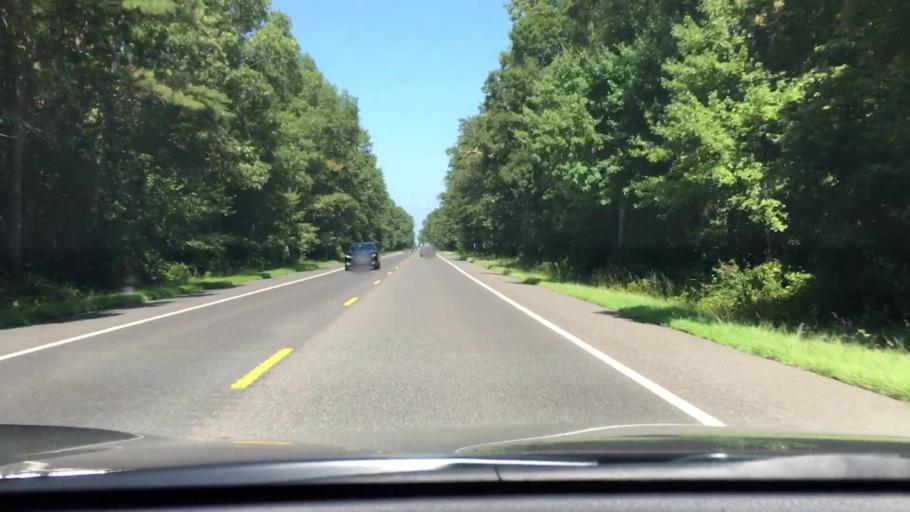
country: US
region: New Jersey
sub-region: Cumberland County
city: Port Norris
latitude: 39.2618
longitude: -74.9330
